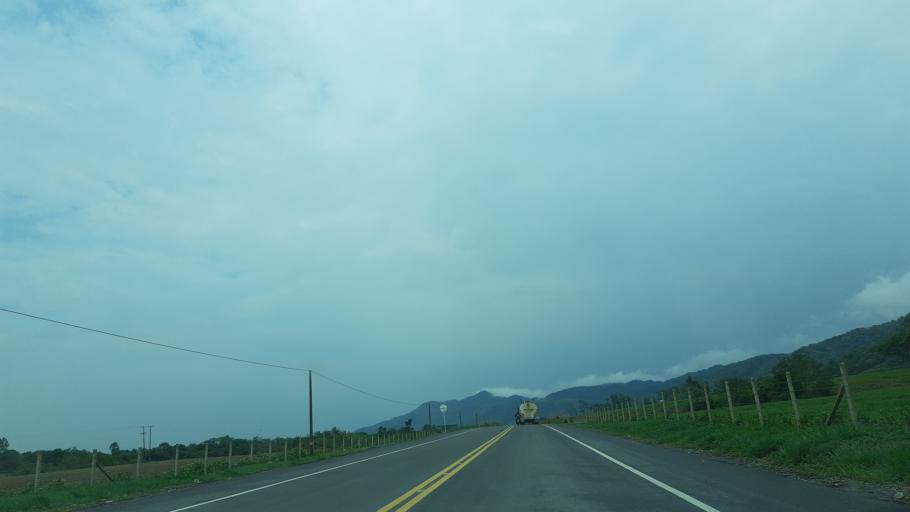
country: CO
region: Casanare
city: Sabanalarga
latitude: 4.7983
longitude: -72.9851
